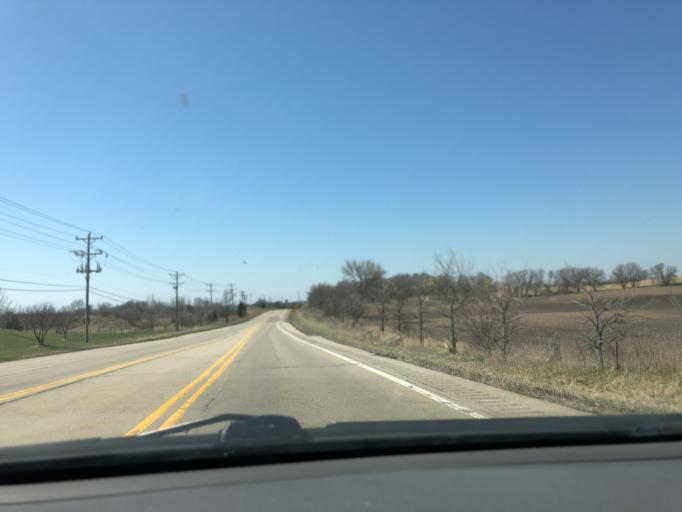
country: US
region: Illinois
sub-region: Kane County
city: Hampshire
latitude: 42.1362
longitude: -88.5005
